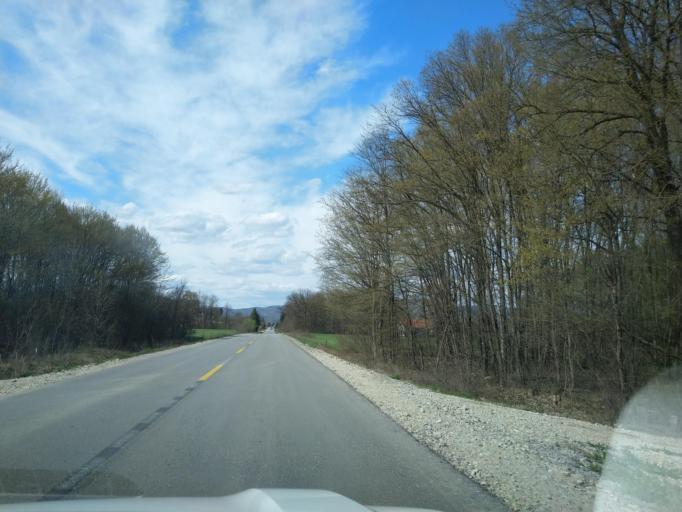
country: RS
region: Central Serbia
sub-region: Zlatiborski Okrug
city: Arilje
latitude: 43.8056
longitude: 20.0932
